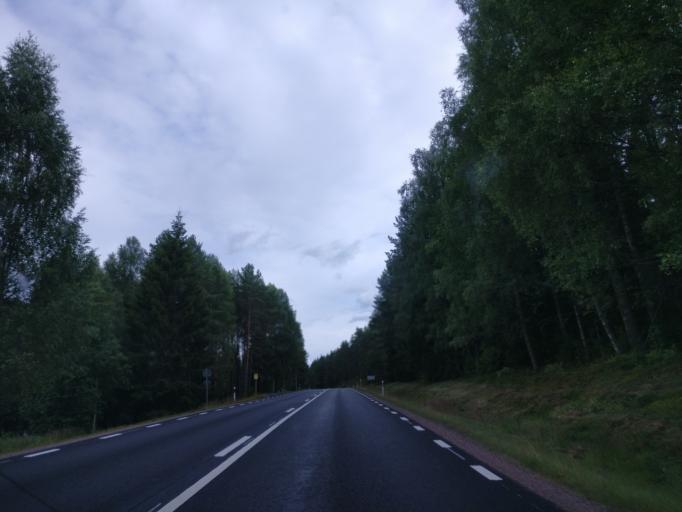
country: SE
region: Vaermland
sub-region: Hagfors Kommun
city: Hagfors
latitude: 60.0586
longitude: 13.5533
